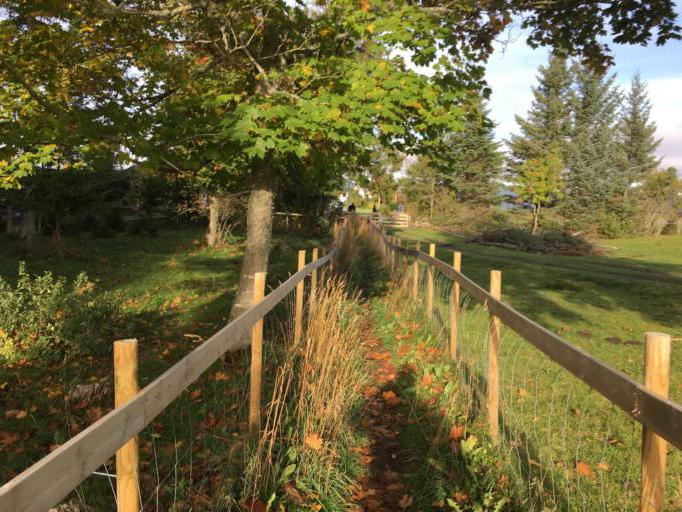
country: NO
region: Nord-Trondelag
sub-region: Leksvik
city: Leksvik
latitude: 63.5743
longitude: 10.6130
